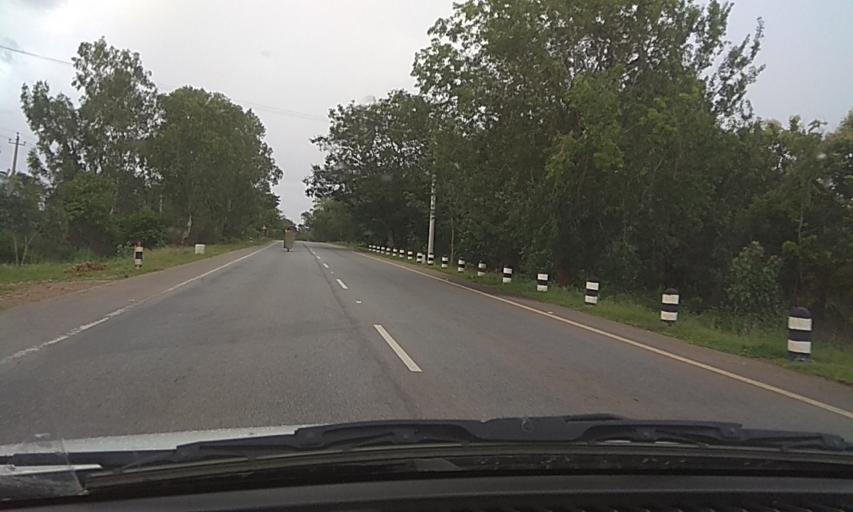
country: IN
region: Karnataka
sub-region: Mandya
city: Maddur
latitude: 12.7976
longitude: 77.0416
